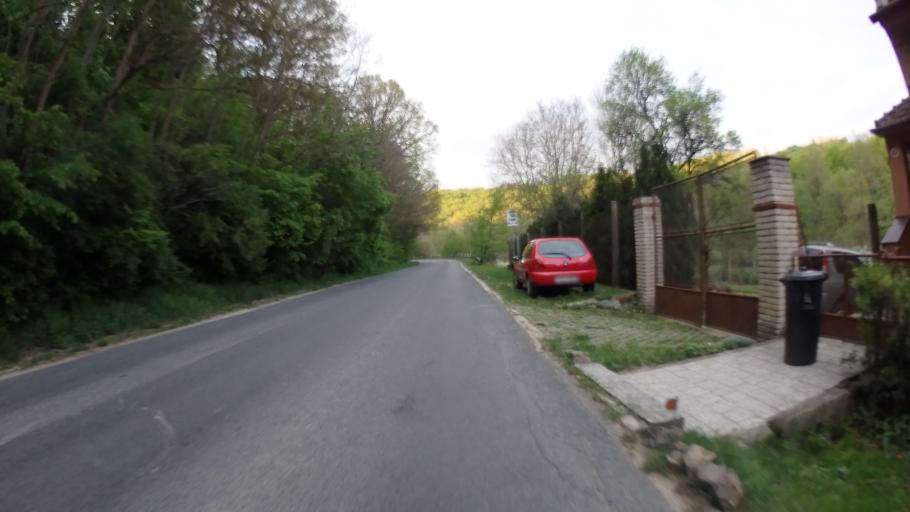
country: CZ
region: South Moravian
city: Strelice
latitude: 49.1435
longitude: 16.4671
